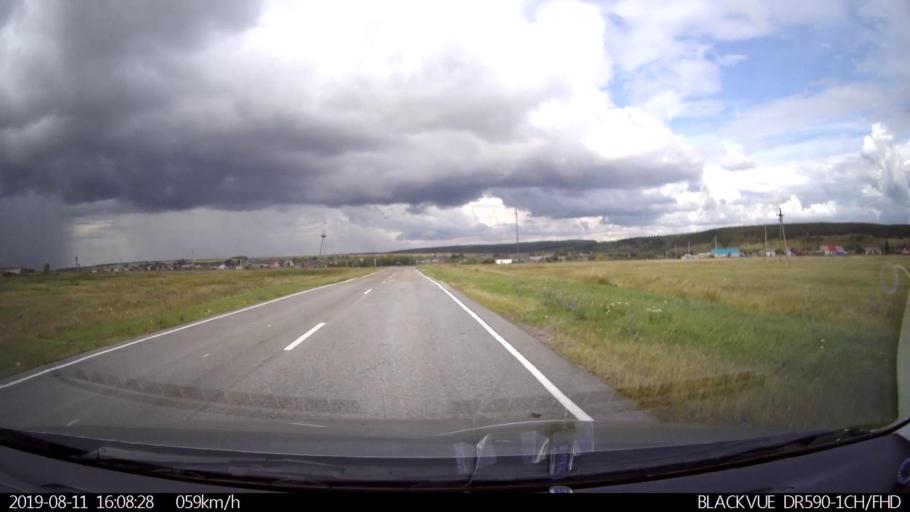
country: RU
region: Ulyanovsk
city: Ignatovka
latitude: 53.9849
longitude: 47.6480
